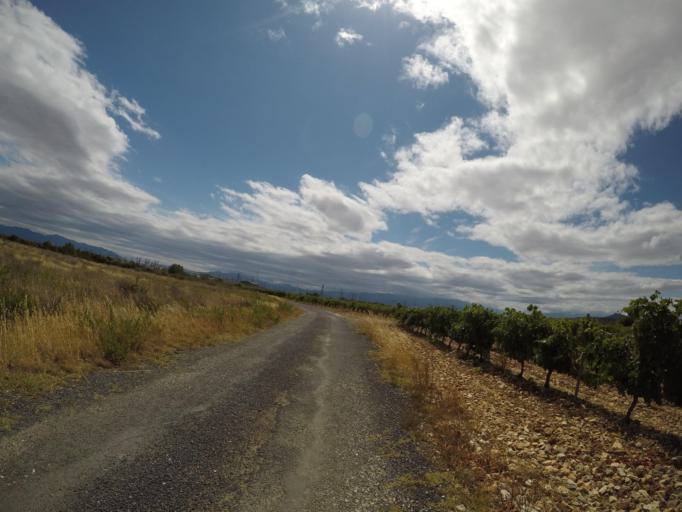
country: FR
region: Languedoc-Roussillon
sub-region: Departement des Pyrenees-Orientales
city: Baixas
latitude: 42.7394
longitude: 2.8032
